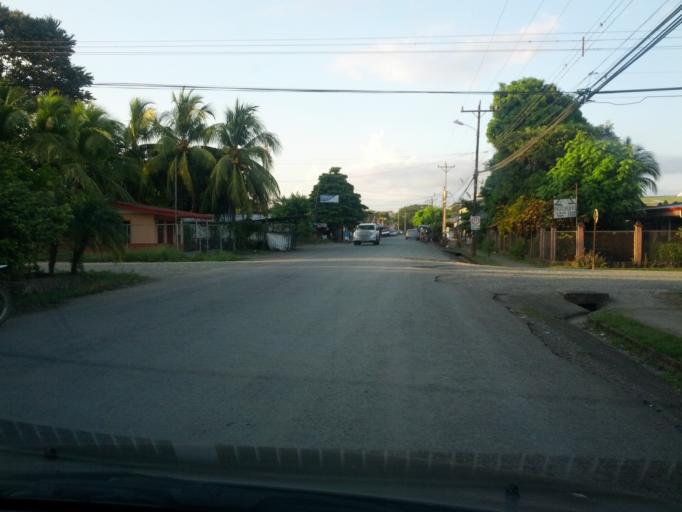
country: CR
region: Puntarenas
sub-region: Canton de Golfito
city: Golfito
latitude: 8.5358
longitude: -83.3057
